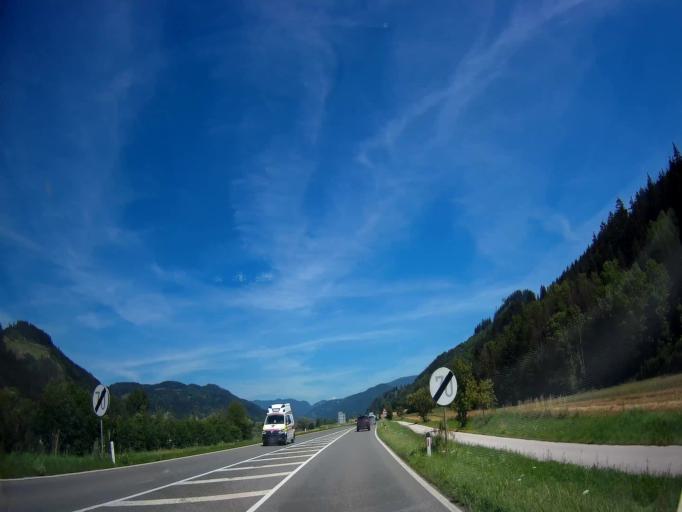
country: AT
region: Carinthia
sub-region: Politischer Bezirk Sankt Veit an der Glan
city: Micheldorf
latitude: 46.9022
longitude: 14.4395
